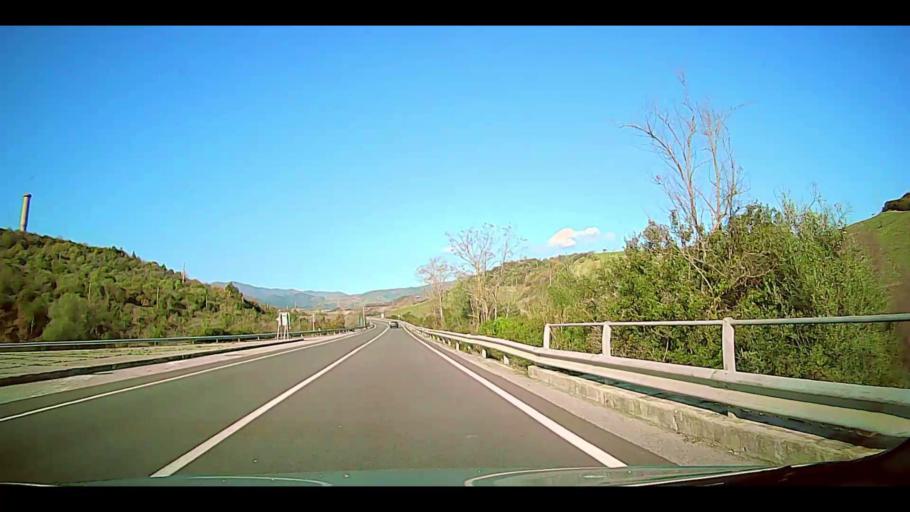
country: IT
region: Calabria
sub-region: Provincia di Crotone
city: Roccabernarda
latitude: 39.1863
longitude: 16.8329
